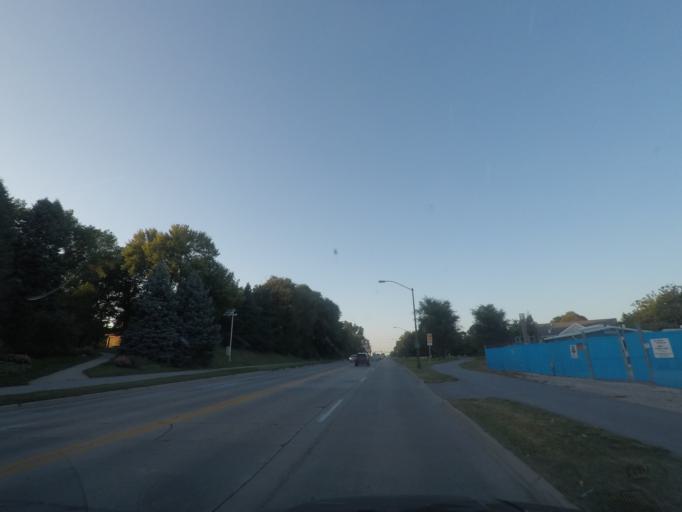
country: US
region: Iowa
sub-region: Story County
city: Ames
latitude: 42.0417
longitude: -93.6448
